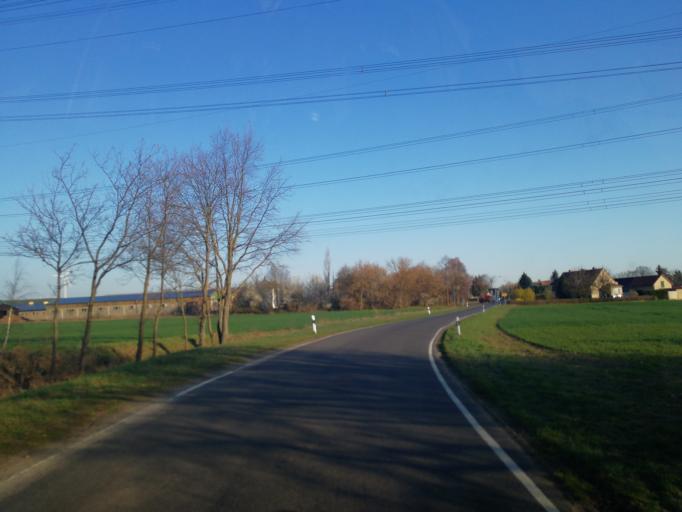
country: DE
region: Brandenburg
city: Drahnsdorf
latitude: 51.8645
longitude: 13.5915
